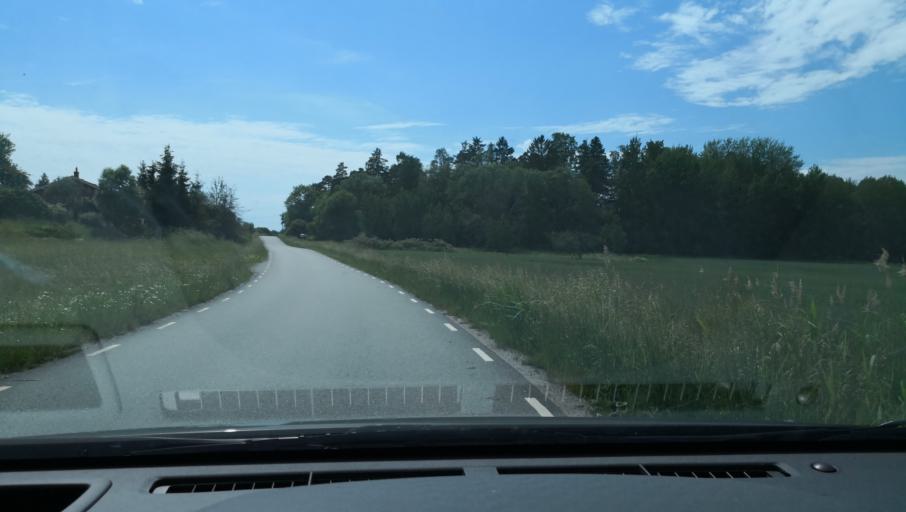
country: SE
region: Uppsala
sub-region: Habo Kommun
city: Balsta
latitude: 59.6898
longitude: 17.4658
